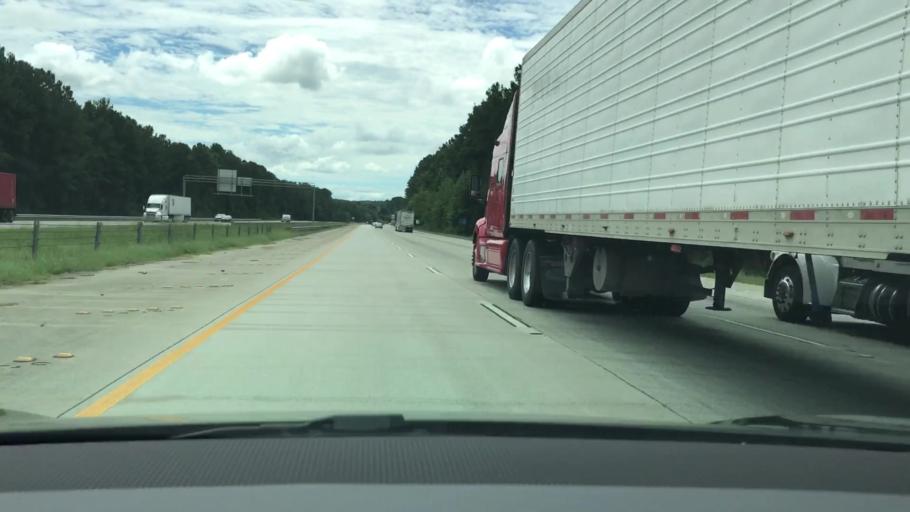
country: US
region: Georgia
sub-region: Coweta County
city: Grantville
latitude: 33.2309
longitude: -84.8092
